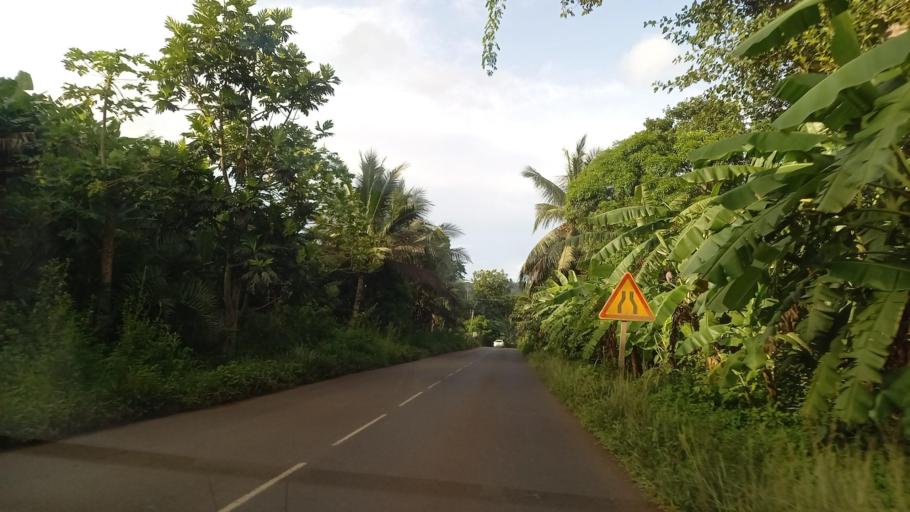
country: YT
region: Bandraboua
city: Bandraboua
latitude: -12.7298
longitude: 45.1199
